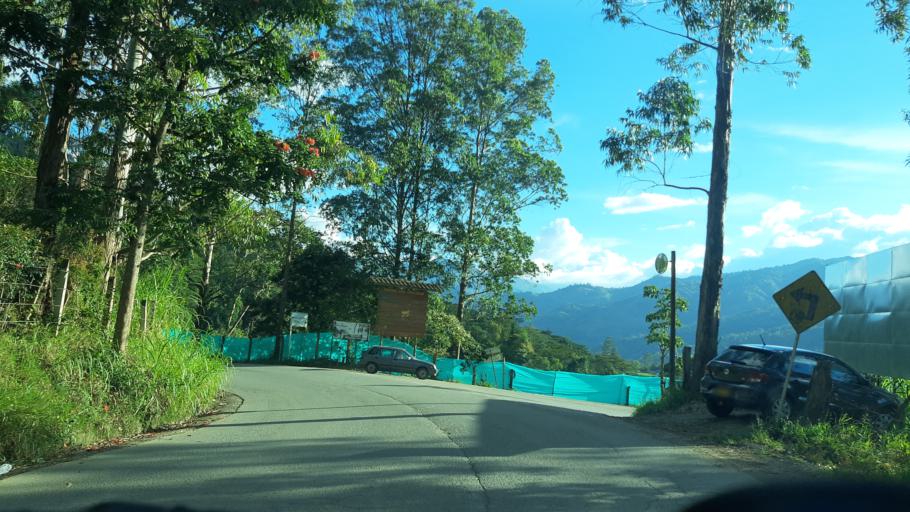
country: CO
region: Boyaca
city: Garagoa
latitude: 5.0746
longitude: -73.3793
